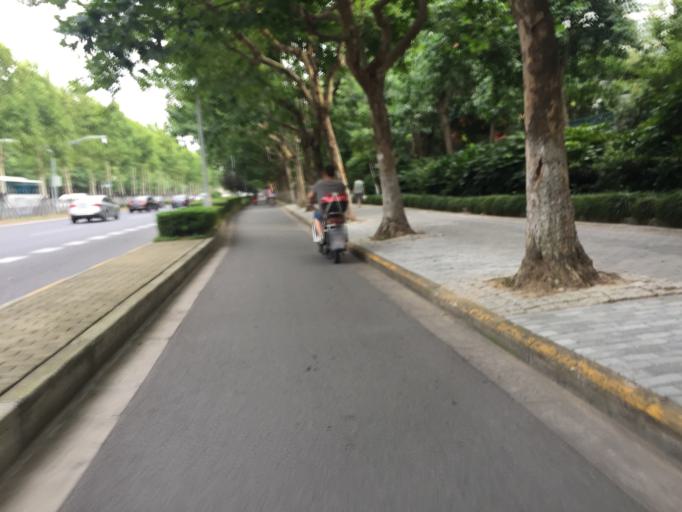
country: CN
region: Shanghai Shi
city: Huamu
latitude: 31.1858
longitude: 121.5366
